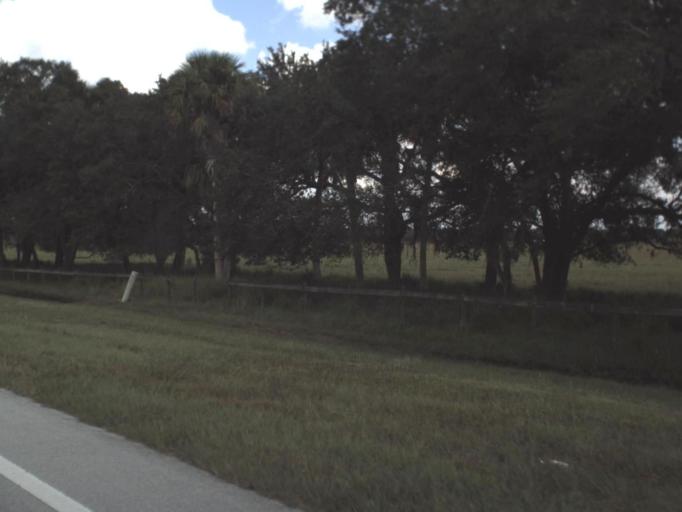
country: US
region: Florida
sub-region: Okeechobee County
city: Okeechobee
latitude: 27.3115
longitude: -80.9056
